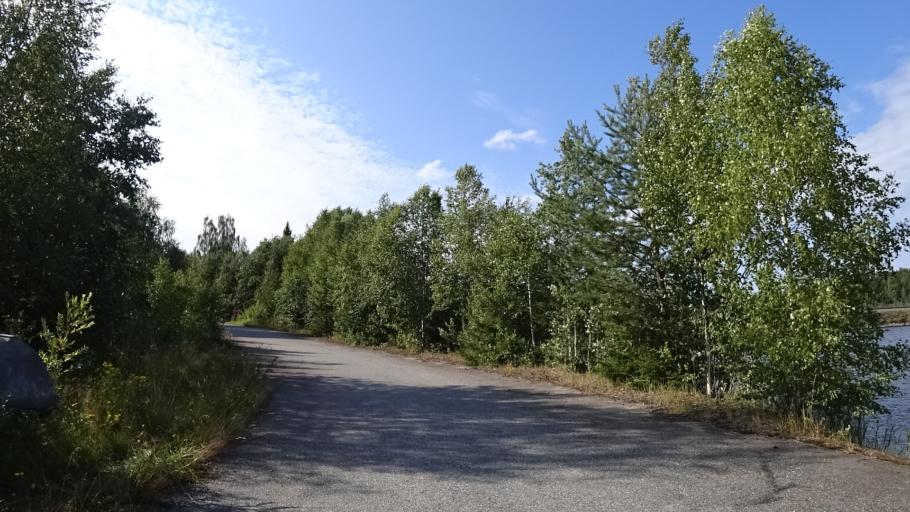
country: FI
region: North Karelia
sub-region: Joensuu
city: Eno
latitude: 62.8011
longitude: 30.1205
